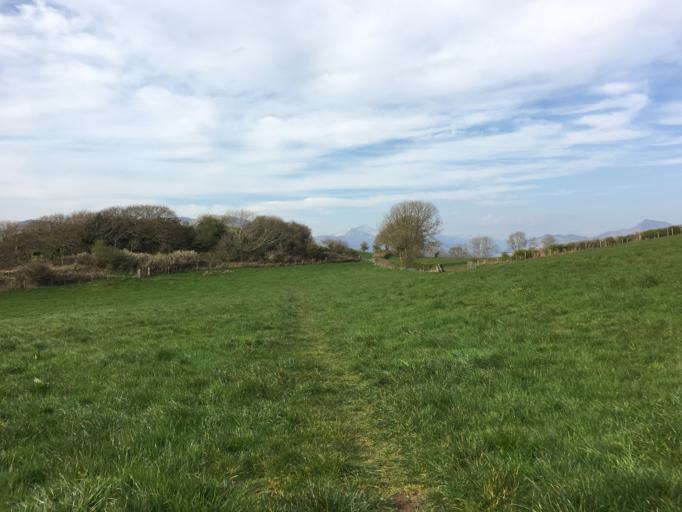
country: GB
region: Wales
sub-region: Gwynedd
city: Porthmadog
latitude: 52.9164
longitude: -4.1051
